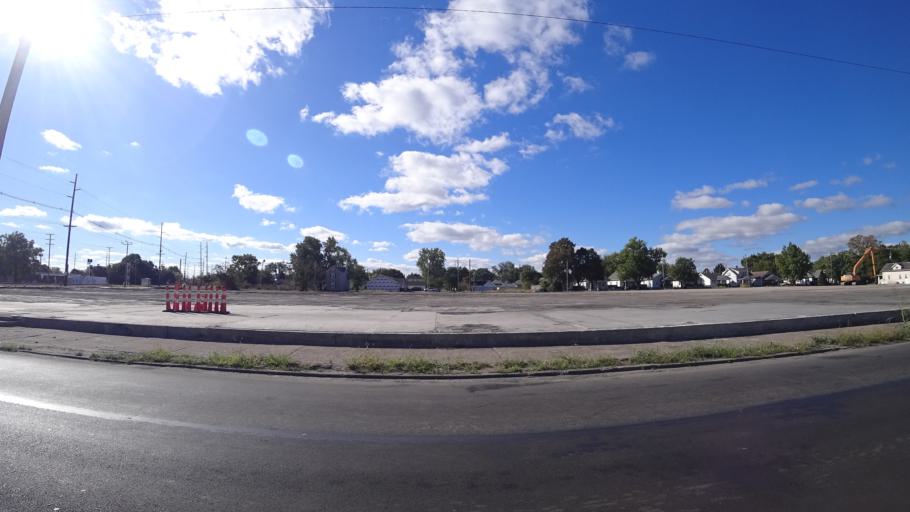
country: US
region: Ohio
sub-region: Butler County
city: Fairfield
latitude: 39.3694
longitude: -84.5507
